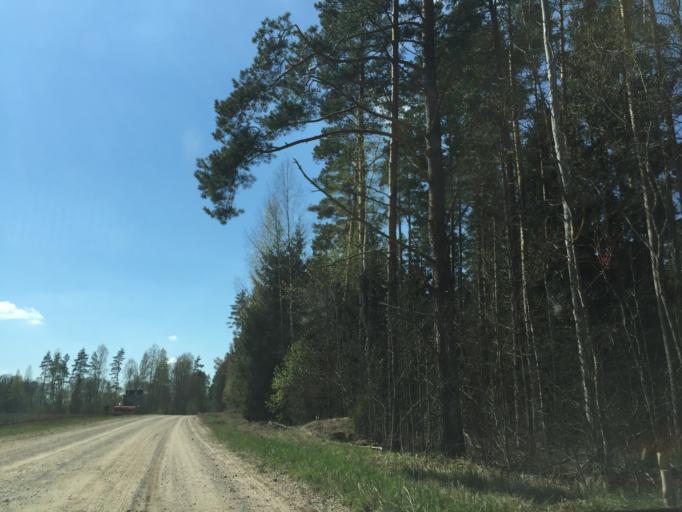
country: LV
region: Smiltene
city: Smiltene
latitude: 57.5683
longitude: 25.9157
